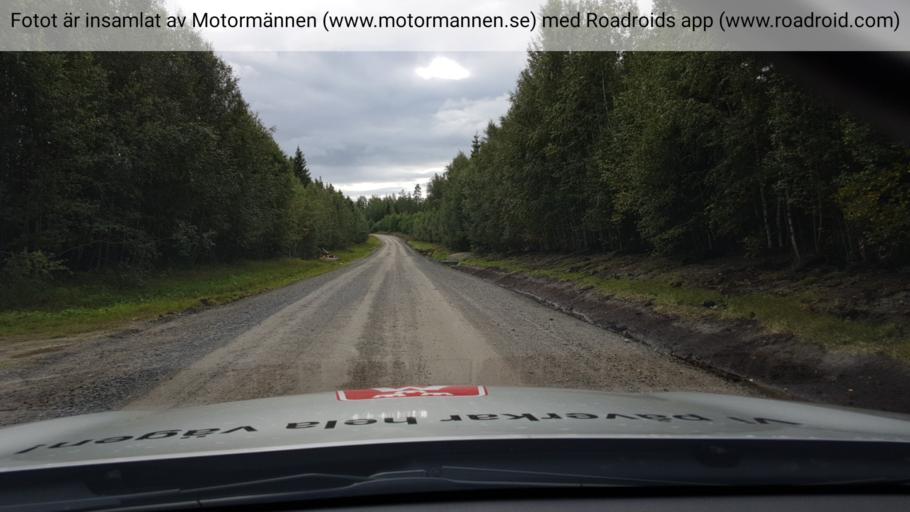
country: SE
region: Jaemtland
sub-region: Ragunda Kommun
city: Hammarstrand
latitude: 62.9322
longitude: 16.1306
